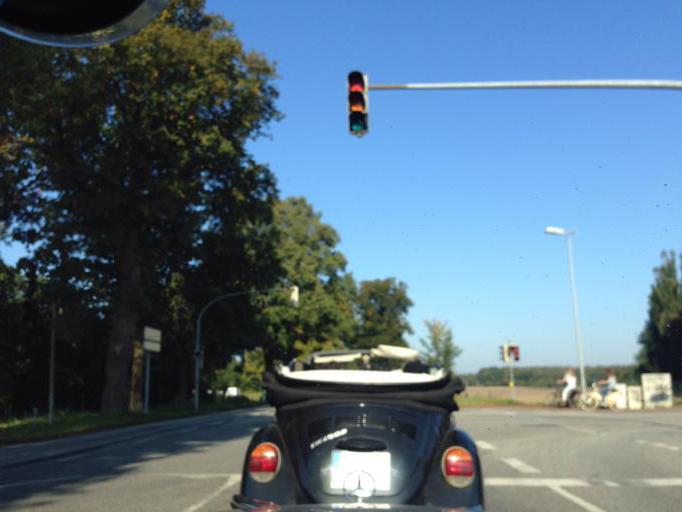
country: DE
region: Schleswig-Holstein
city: Ahrensburg
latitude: 53.6454
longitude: 10.2012
